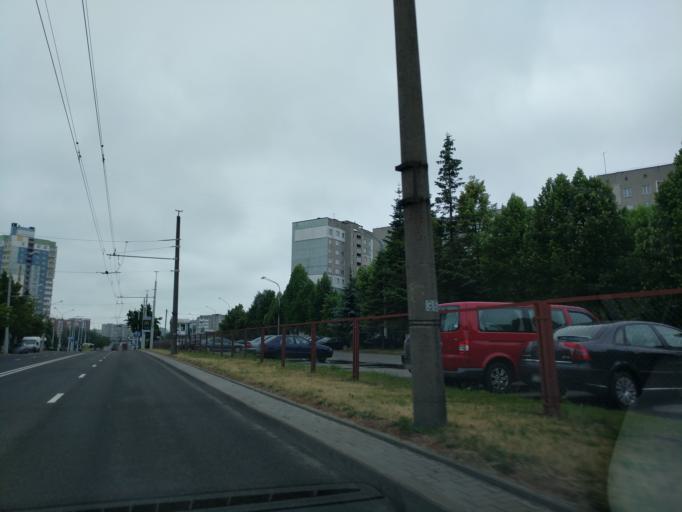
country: BY
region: Minsk
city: Novoye Medvezhino
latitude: 53.8676
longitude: 27.4714
